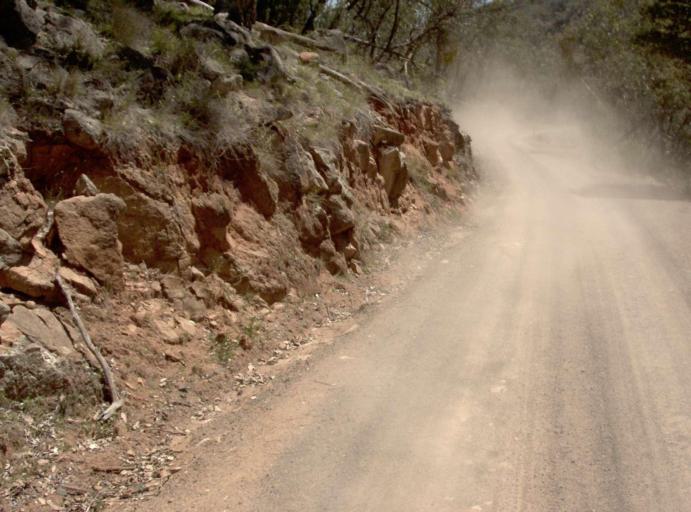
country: AU
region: New South Wales
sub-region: Snowy River
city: Jindabyne
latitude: -37.0552
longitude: 148.5357
